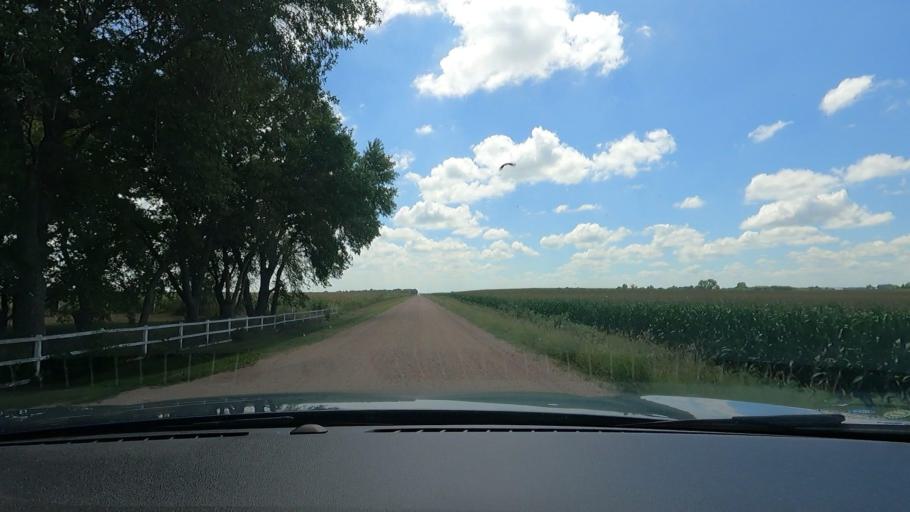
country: US
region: Nebraska
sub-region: Saunders County
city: Wahoo
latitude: 41.2773
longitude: -96.5419
